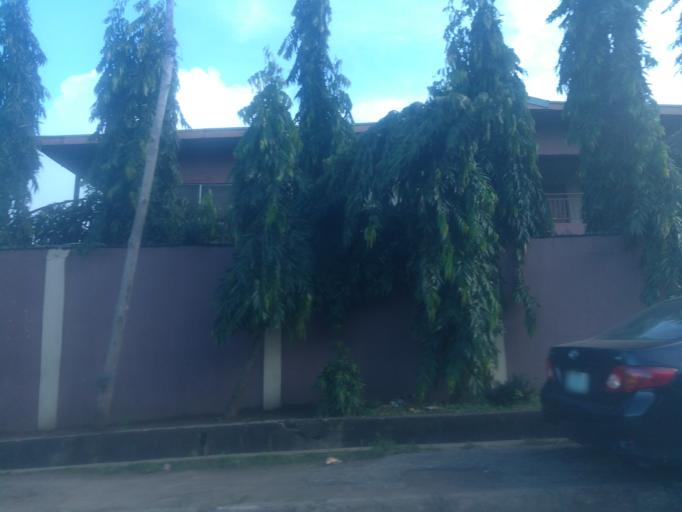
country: NG
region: Lagos
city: Ikeja
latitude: 6.6265
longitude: 3.3565
